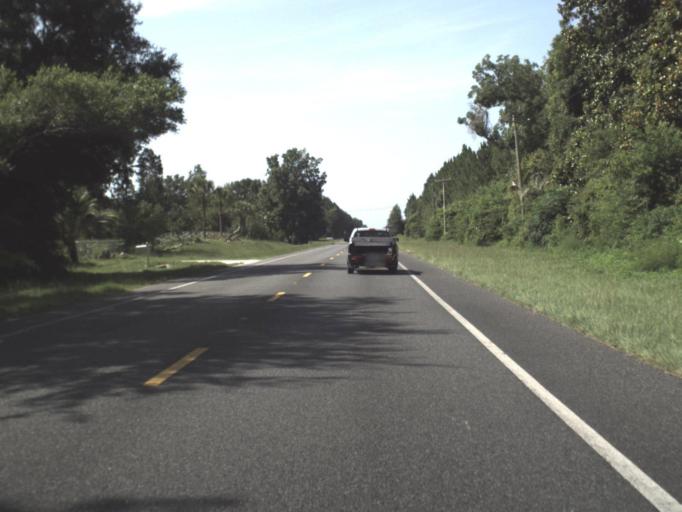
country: US
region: Florida
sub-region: Gilchrist County
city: Trenton
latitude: 29.5520
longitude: -82.8229
